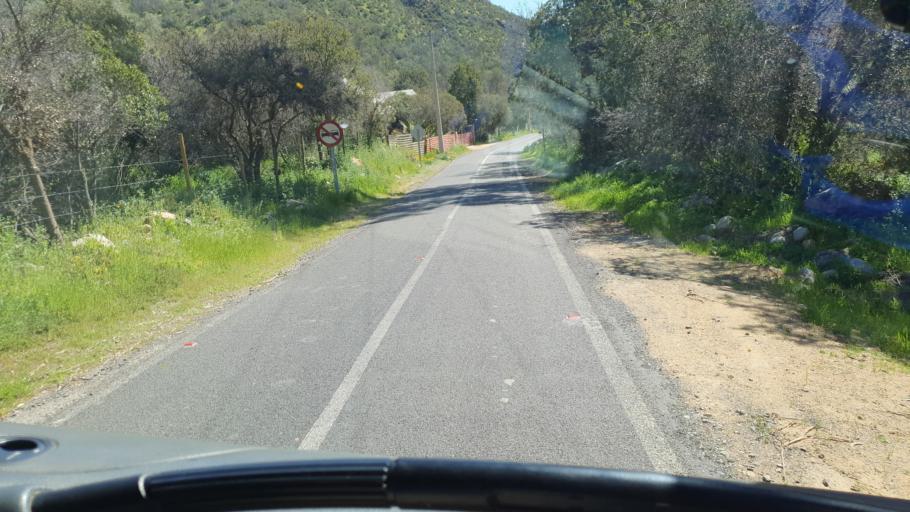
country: CL
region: Valparaiso
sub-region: Provincia de Marga Marga
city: Limache
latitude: -33.1835
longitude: -71.1087
